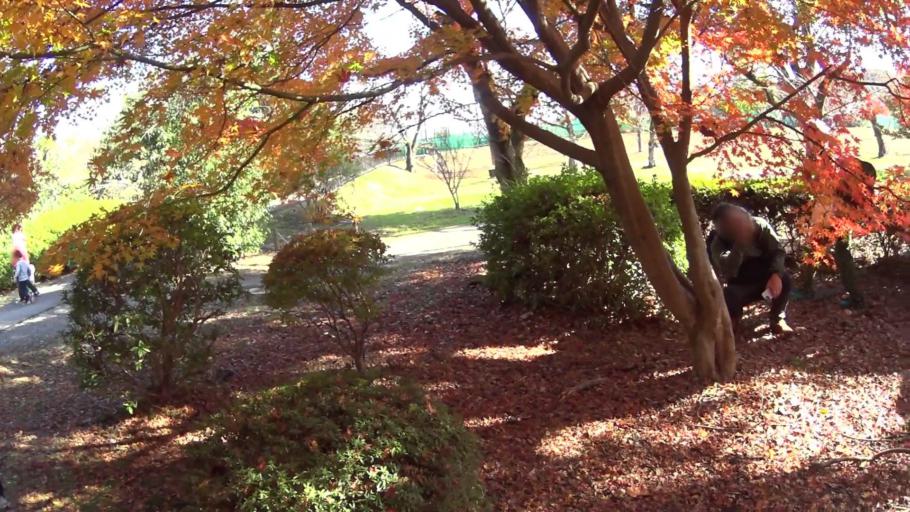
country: JP
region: Kyoto
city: Uji
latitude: 34.9399
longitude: 135.7772
